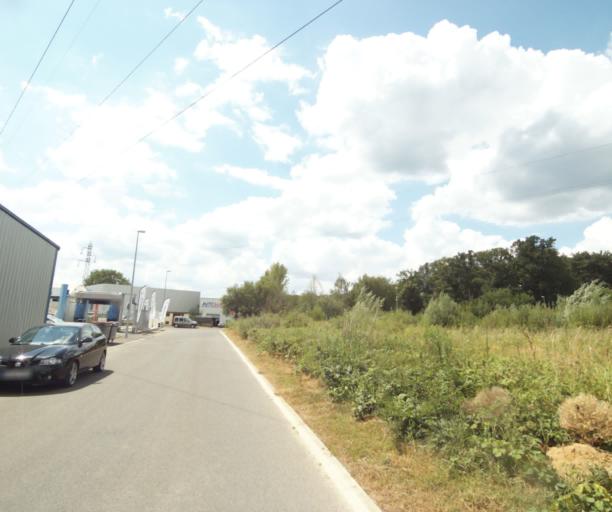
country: FR
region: Ile-de-France
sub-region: Departement de Seine-et-Marne
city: Vulaines-sur-Seine
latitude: 48.4246
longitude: 2.7696
